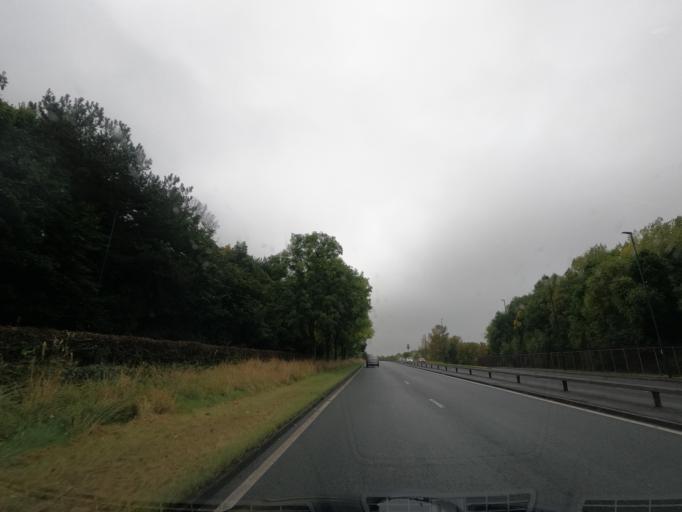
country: GB
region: England
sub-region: Redcar and Cleveland
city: South Bank
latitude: 54.5739
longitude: -1.1017
